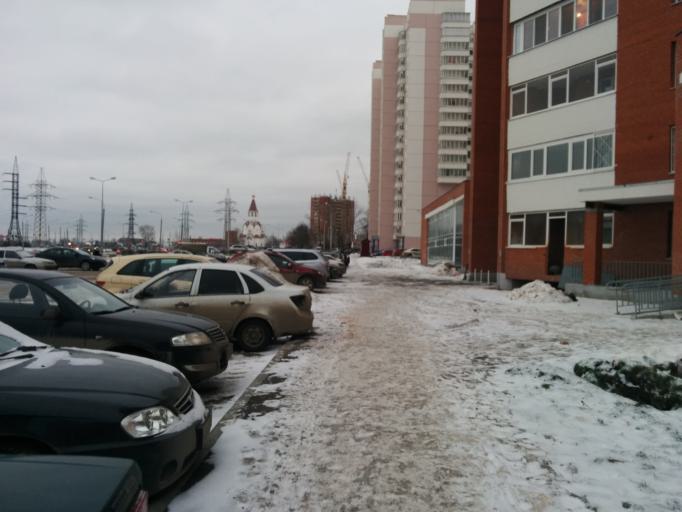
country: RU
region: Perm
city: Perm
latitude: 57.9865
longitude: 56.2877
